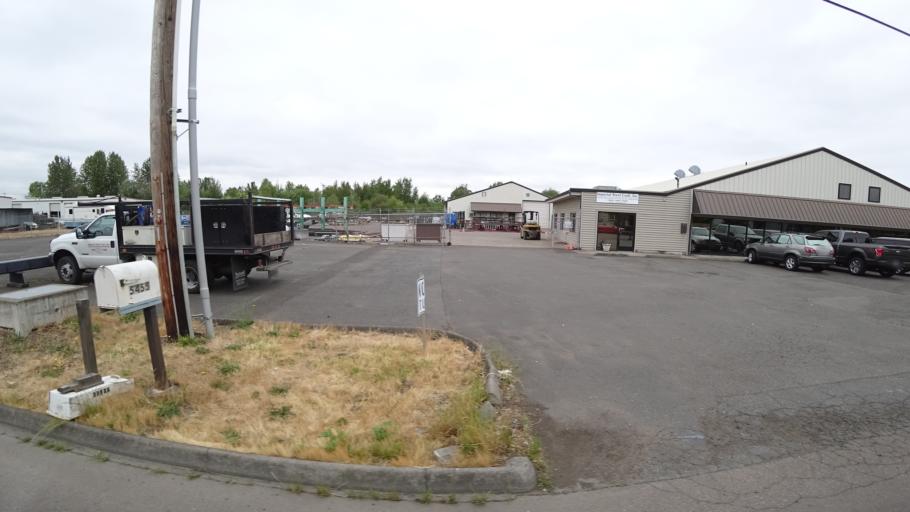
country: US
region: Oregon
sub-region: Washington County
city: Aloha
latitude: 45.4976
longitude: -122.9269
